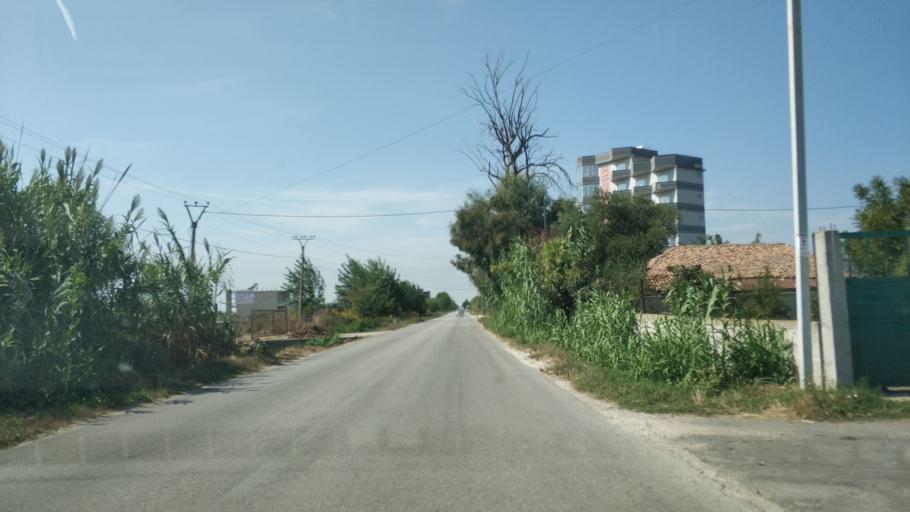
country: AL
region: Fier
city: Fier
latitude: 40.7339
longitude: 19.5299
